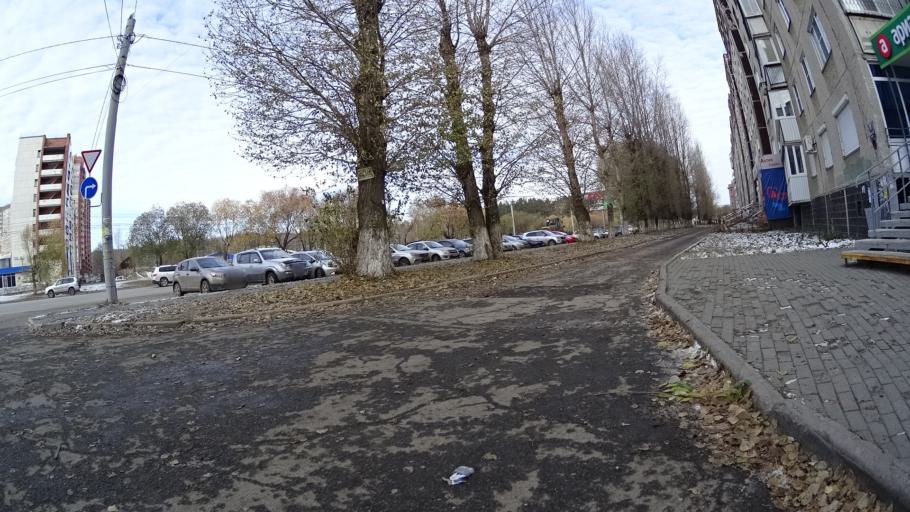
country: RU
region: Chelyabinsk
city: Roshchino
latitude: 55.1906
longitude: 61.2957
